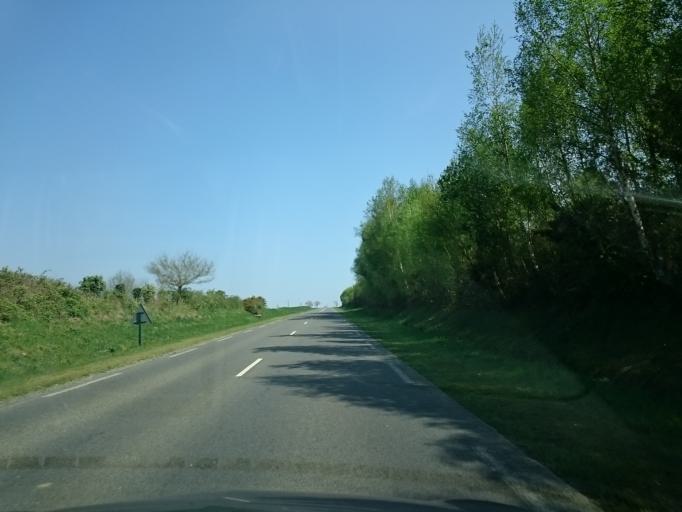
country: FR
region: Brittany
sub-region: Departement d'Ille-et-Vilaine
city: Nouvoitou
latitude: 48.0441
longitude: -1.5499
